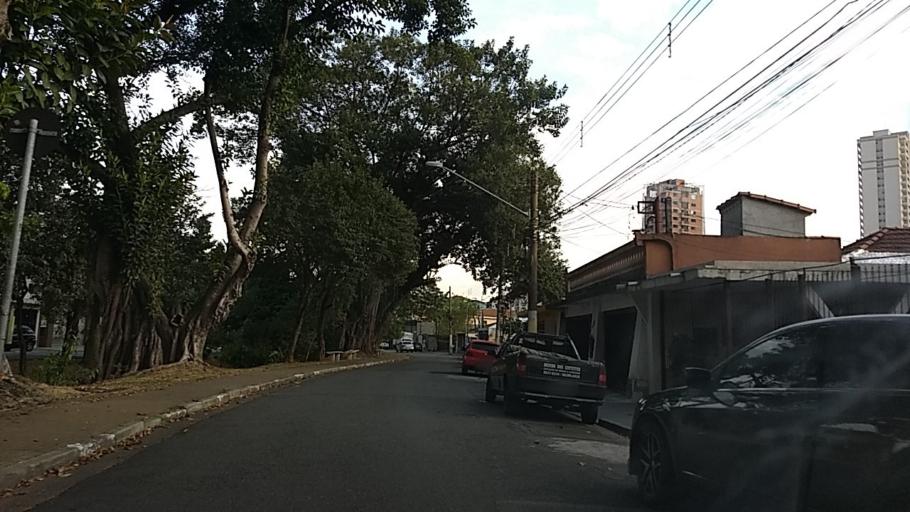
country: BR
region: Sao Paulo
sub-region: Guarulhos
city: Guarulhos
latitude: -23.5103
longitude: -46.5791
